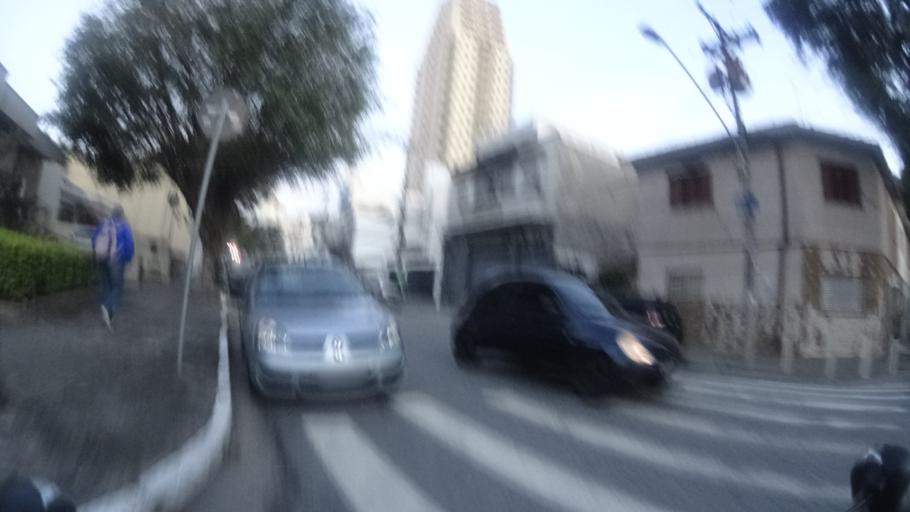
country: BR
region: Sao Paulo
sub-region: Sao Paulo
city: Sao Paulo
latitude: -23.5124
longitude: -46.6633
